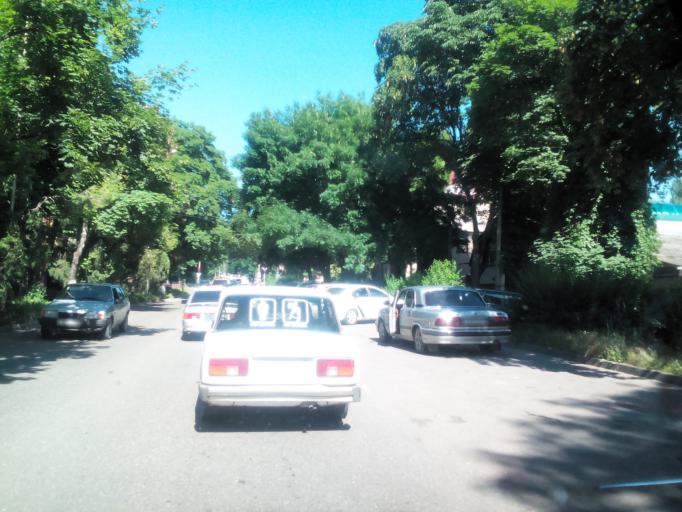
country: RU
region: Stavropol'skiy
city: Pyatigorsk
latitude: 44.0440
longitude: 43.0645
